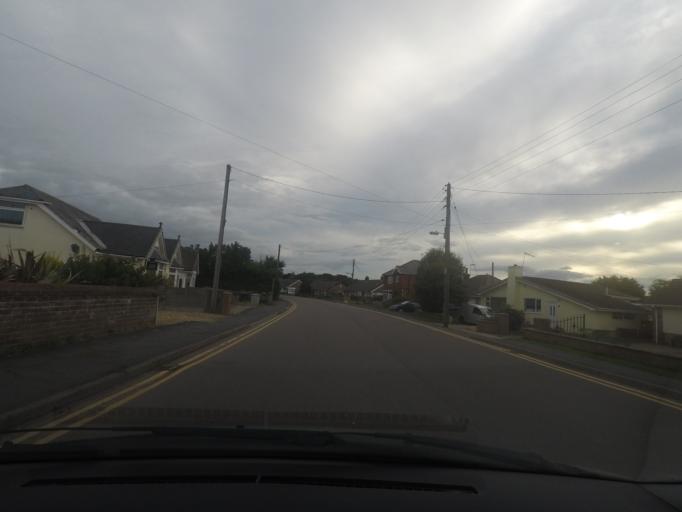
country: GB
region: England
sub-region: Lincolnshire
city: Chapel Saint Leonards
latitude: 53.2227
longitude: 0.3360
